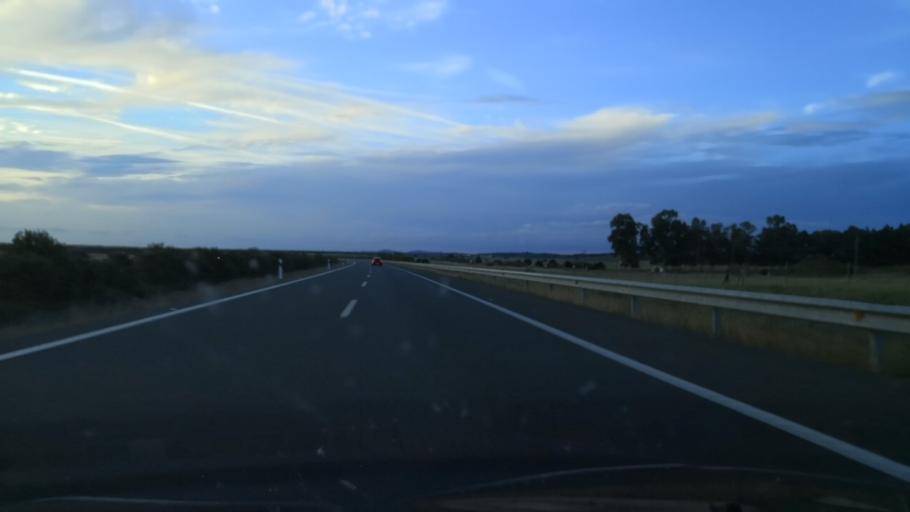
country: ES
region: Extremadura
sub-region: Provincia de Caceres
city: Casas de Don Antonio
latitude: 39.2489
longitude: -6.3071
